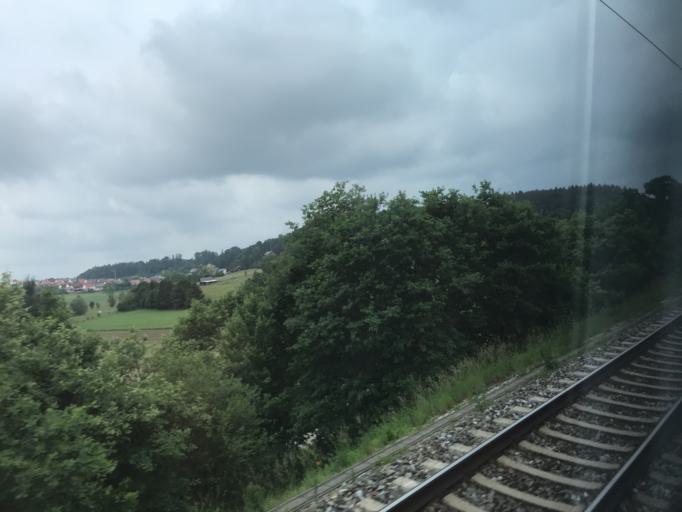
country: DE
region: Bavaria
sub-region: Swabia
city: Dinkelscherben
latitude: 48.3627
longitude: 10.5584
